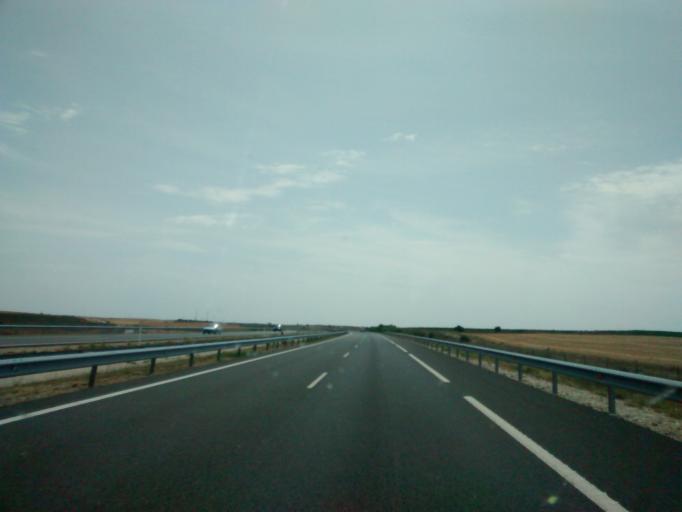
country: ES
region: Castille and Leon
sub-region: Provincia de Burgos
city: Isar
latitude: 42.3725
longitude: -3.9009
